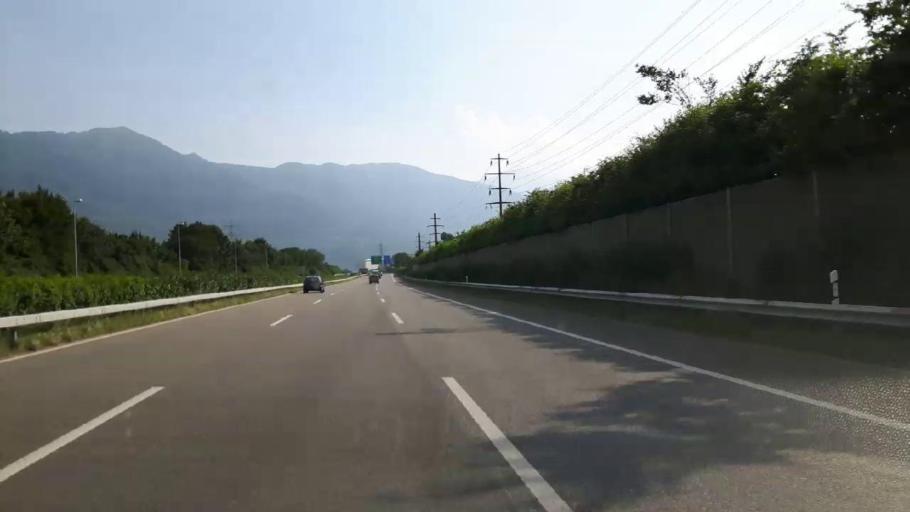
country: CH
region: Ticino
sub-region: Bellinzona District
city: Monte Carasso
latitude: 46.1807
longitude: 8.9995
